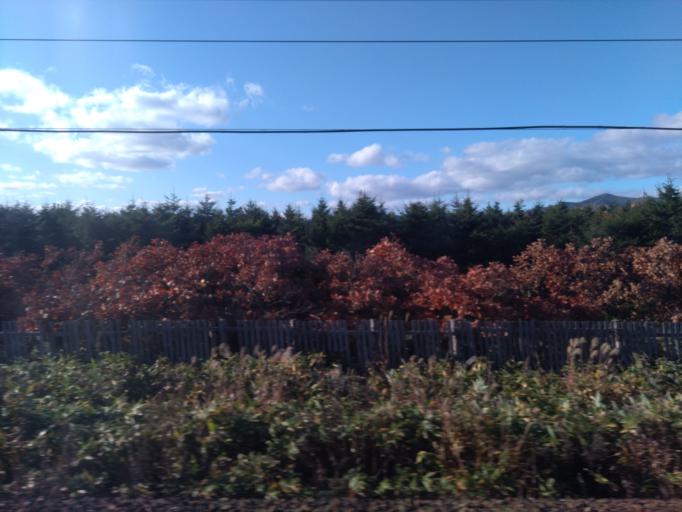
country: JP
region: Hokkaido
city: Niseko Town
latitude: 42.5455
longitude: 140.4118
